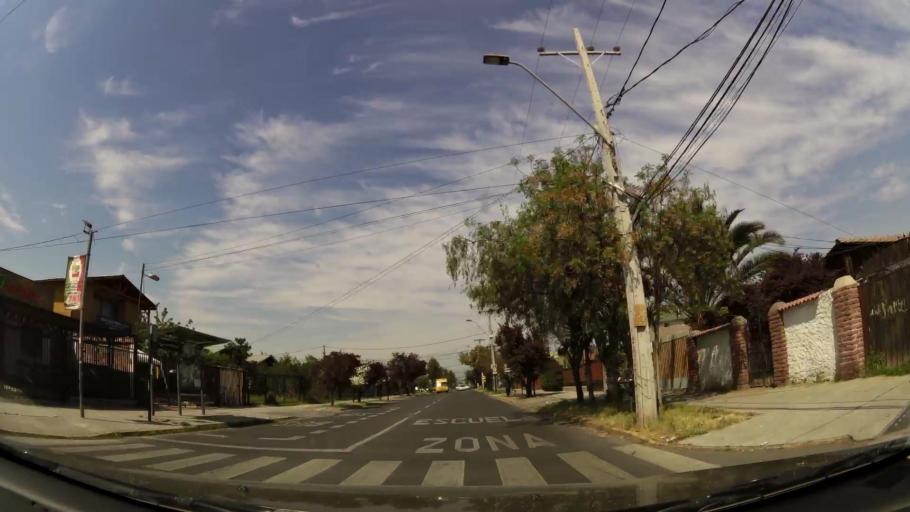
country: CL
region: Santiago Metropolitan
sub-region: Provincia de Cordillera
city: Puente Alto
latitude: -33.5885
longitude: -70.5860
